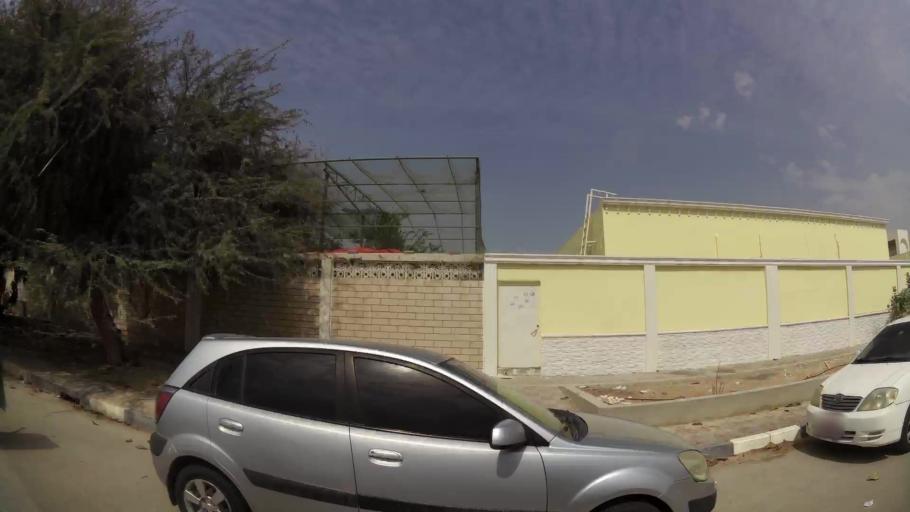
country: AE
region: Abu Dhabi
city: Abu Dhabi
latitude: 24.5249
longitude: 54.6837
